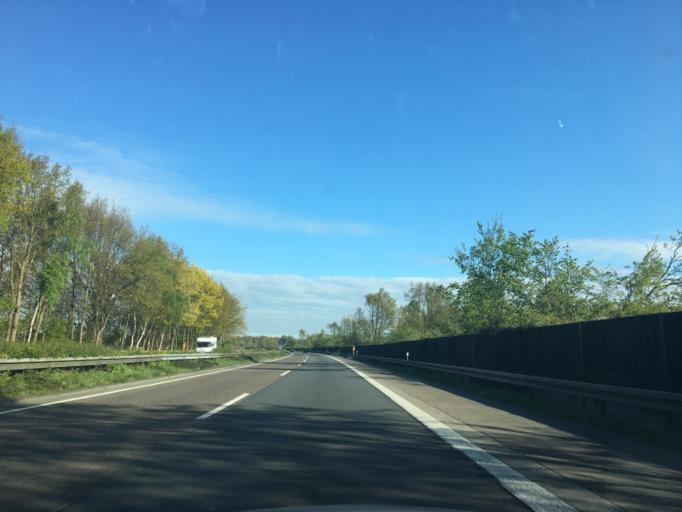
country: DE
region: North Rhine-Westphalia
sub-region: Regierungsbezirk Dusseldorf
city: Hamminkeln
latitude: 51.7365
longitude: 6.6109
